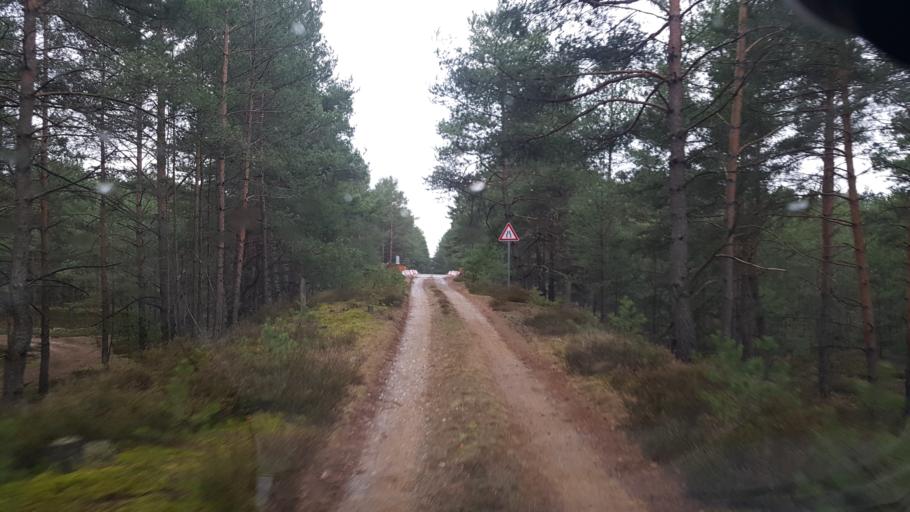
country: DE
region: Brandenburg
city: Crinitz
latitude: 51.6726
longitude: 13.8223
